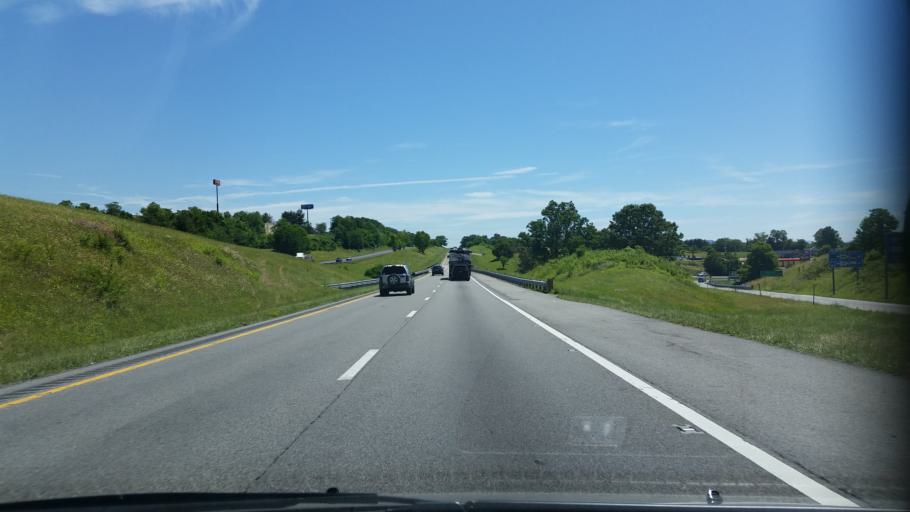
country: US
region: Virginia
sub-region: Wythe County
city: Wytheville
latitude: 36.9593
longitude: -81.1012
